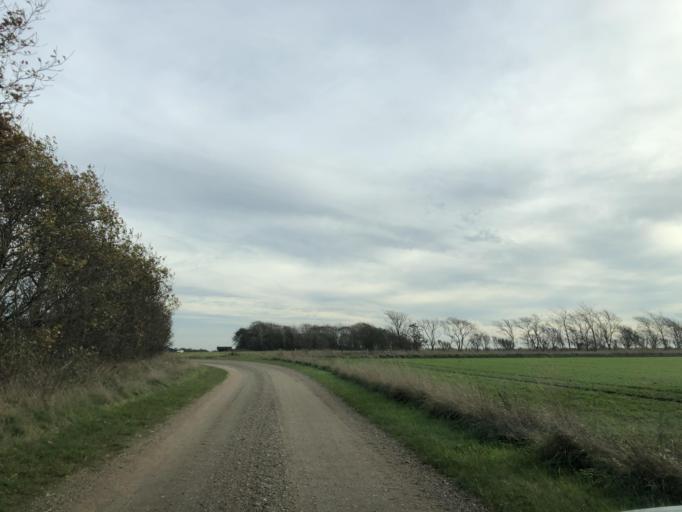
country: DK
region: South Denmark
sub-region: Tonder Kommune
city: Sherrebek
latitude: 55.1806
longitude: 8.7022
